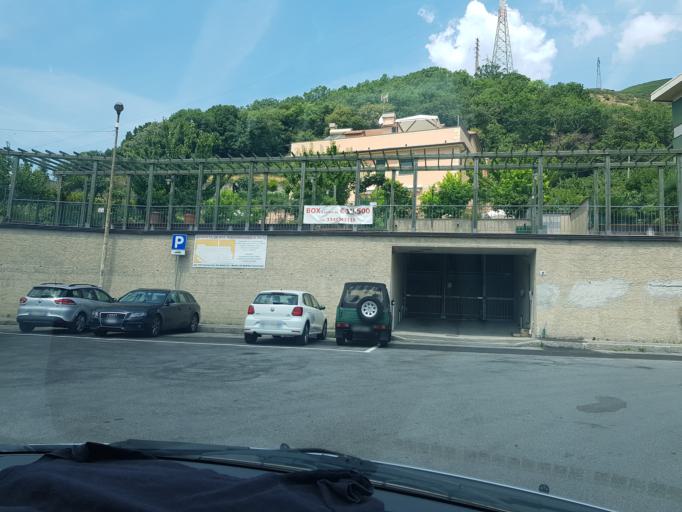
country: IT
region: Liguria
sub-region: Provincia di Genova
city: San Teodoro
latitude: 44.4360
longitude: 8.8695
